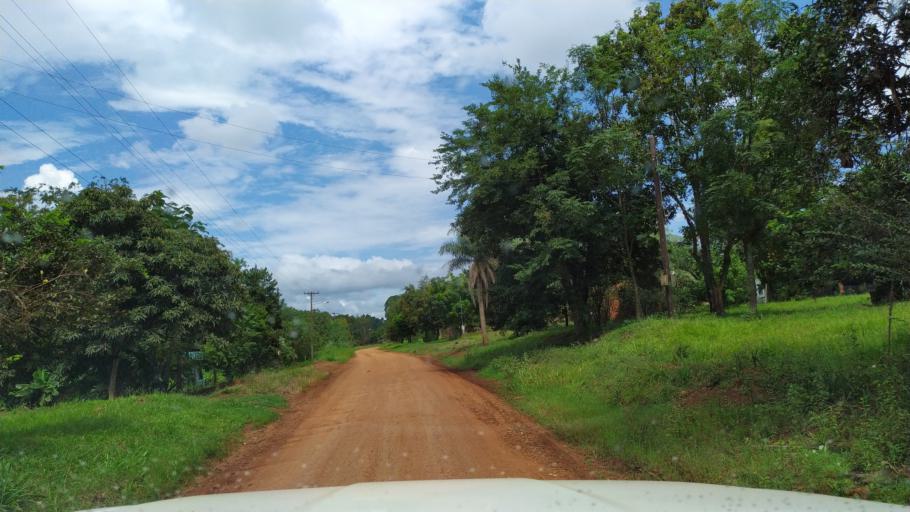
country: AR
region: Misiones
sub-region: Departamento de Eldorado
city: Eldorado
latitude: -26.5115
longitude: -54.5914
